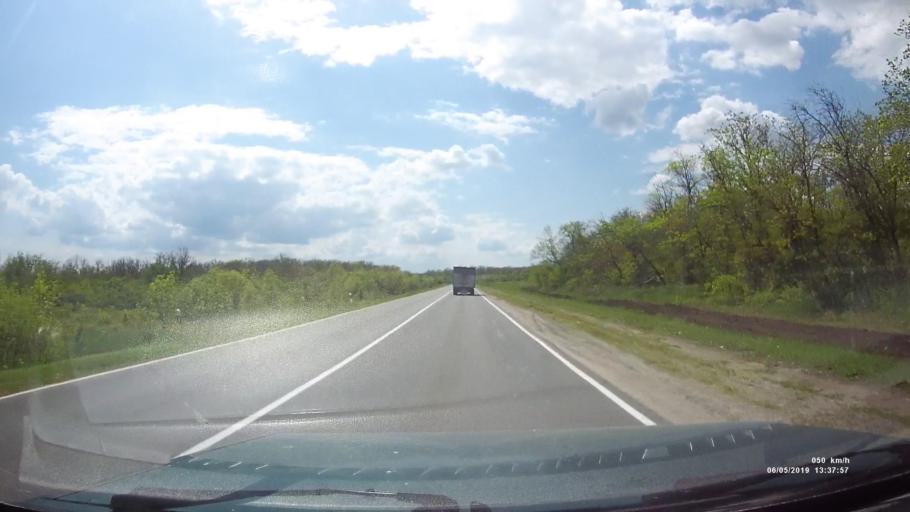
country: RU
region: Rostov
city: Ust'-Donetskiy
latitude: 47.6887
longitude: 40.7144
